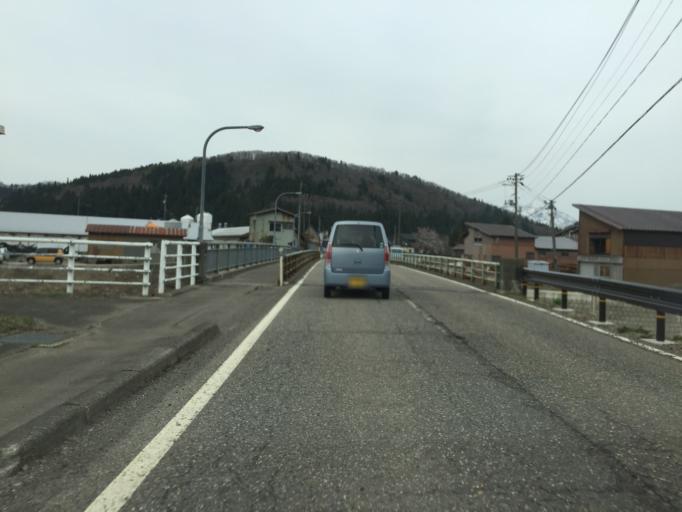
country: JP
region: Niigata
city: Tochio-honcho
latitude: 37.5068
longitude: 139.0358
